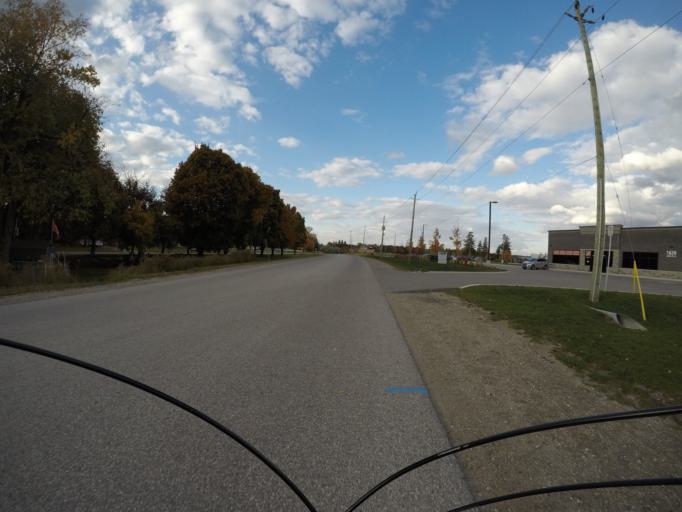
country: CA
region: Ontario
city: Waterloo
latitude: 43.5482
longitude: -80.5525
